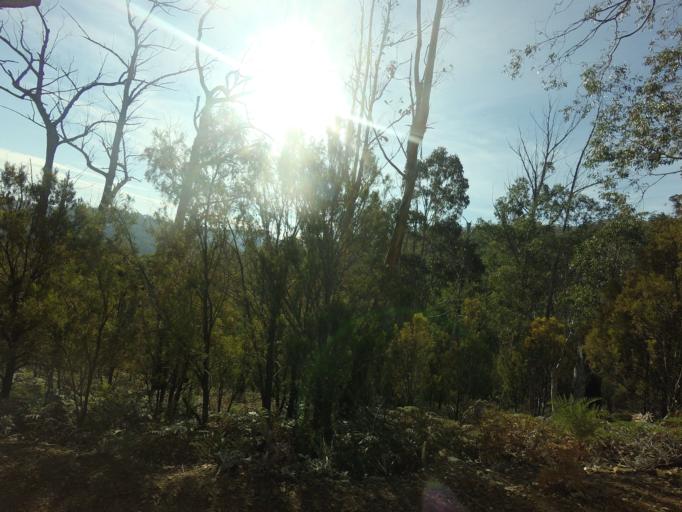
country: AU
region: Tasmania
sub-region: Sorell
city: Sorell
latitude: -42.5269
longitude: 147.4596
